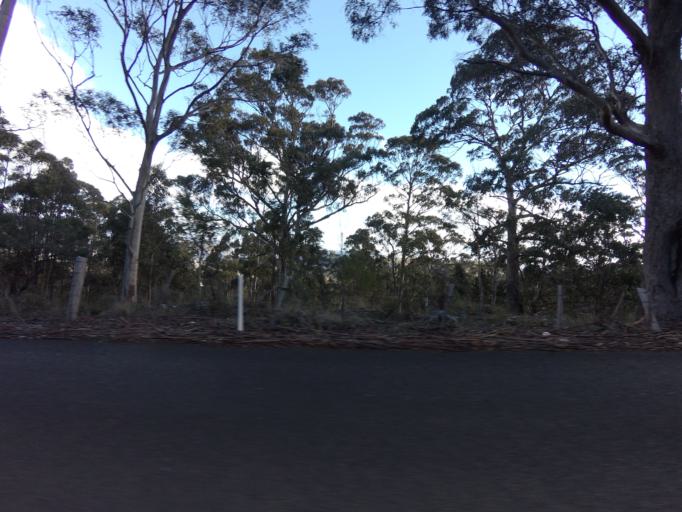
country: AU
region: Tasmania
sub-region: Derwent Valley
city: New Norfolk
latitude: -42.7292
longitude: 147.0316
